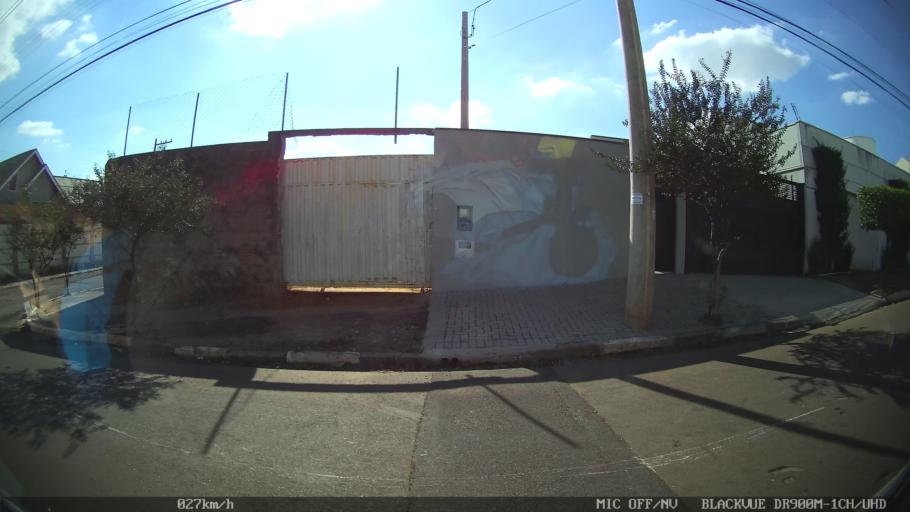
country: BR
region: Sao Paulo
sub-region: Sumare
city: Sumare
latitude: -22.8231
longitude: -47.2789
